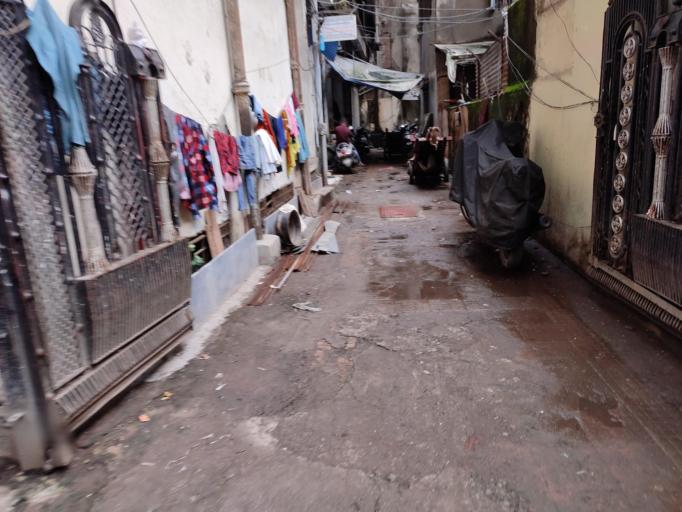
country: IN
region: Maharashtra
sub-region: Mumbai Suburban
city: Mumbai
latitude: 18.9559
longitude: 72.8256
